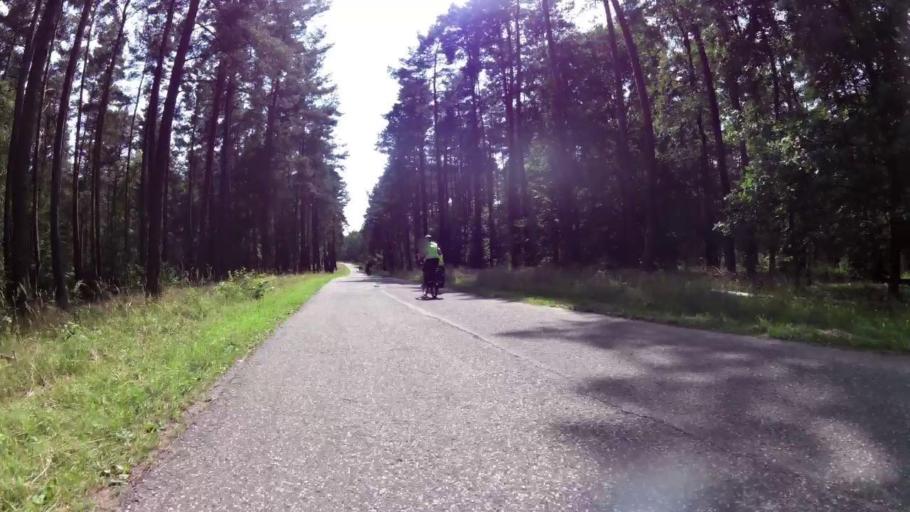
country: PL
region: West Pomeranian Voivodeship
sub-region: Powiat choszczenski
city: Drawno
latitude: 53.3303
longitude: 15.6955
